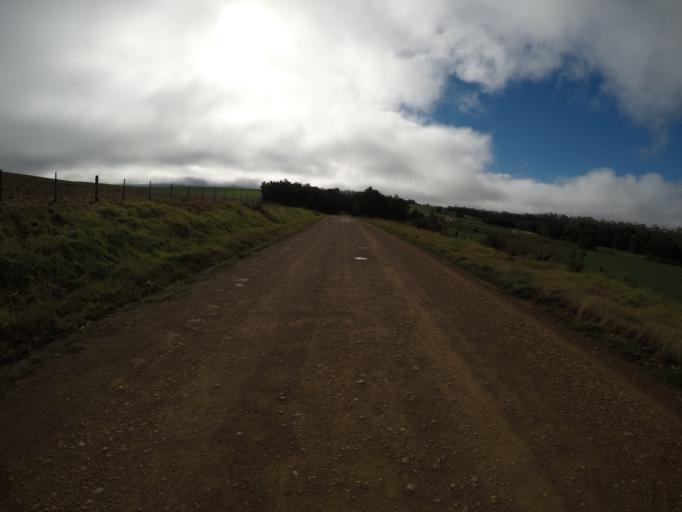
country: ZA
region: Western Cape
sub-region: Overberg District Municipality
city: Caledon
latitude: -34.1154
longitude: 19.7901
